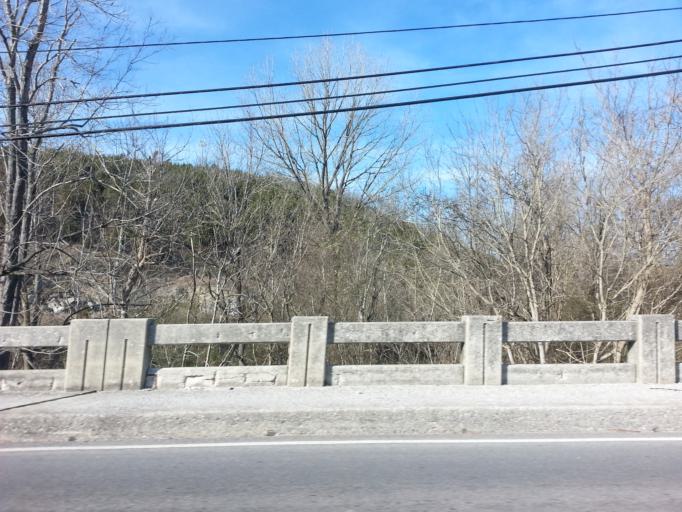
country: US
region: Tennessee
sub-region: Cannon County
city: Woodbury
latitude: 35.8282
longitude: -86.0764
